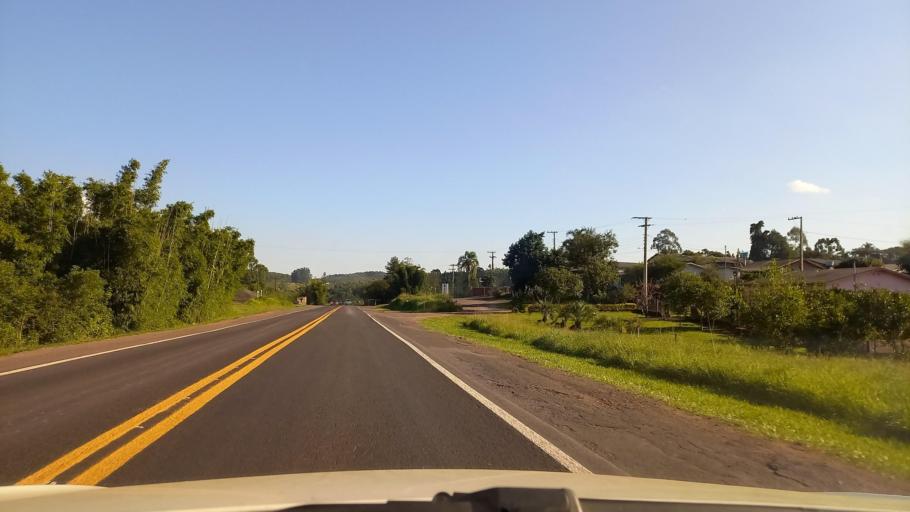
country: BR
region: Rio Grande do Sul
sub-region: Taquari
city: Taquari
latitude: -29.6962
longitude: -51.7489
